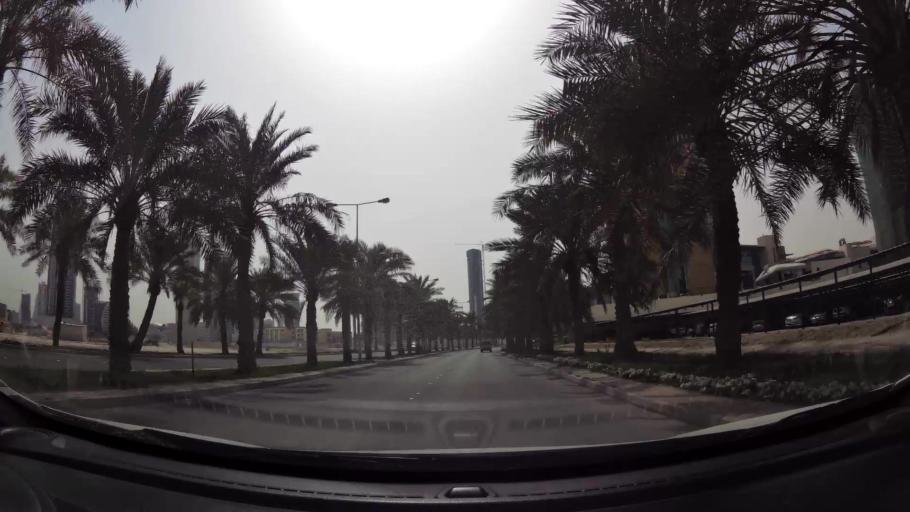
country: BH
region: Manama
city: Jidd Hafs
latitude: 26.2368
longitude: 50.5432
